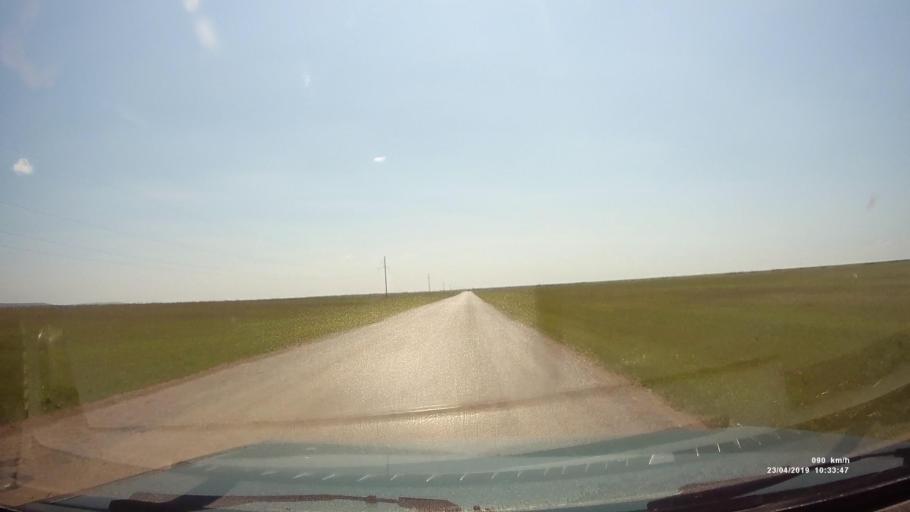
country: RU
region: Kalmykiya
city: Yashalta
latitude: 46.5703
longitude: 42.6017
